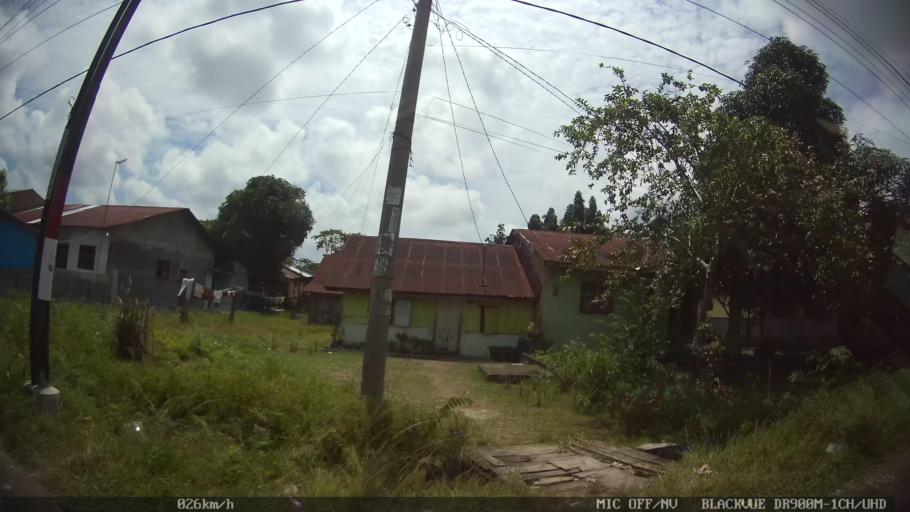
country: ID
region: North Sumatra
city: Medan
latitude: 3.6152
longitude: 98.7628
